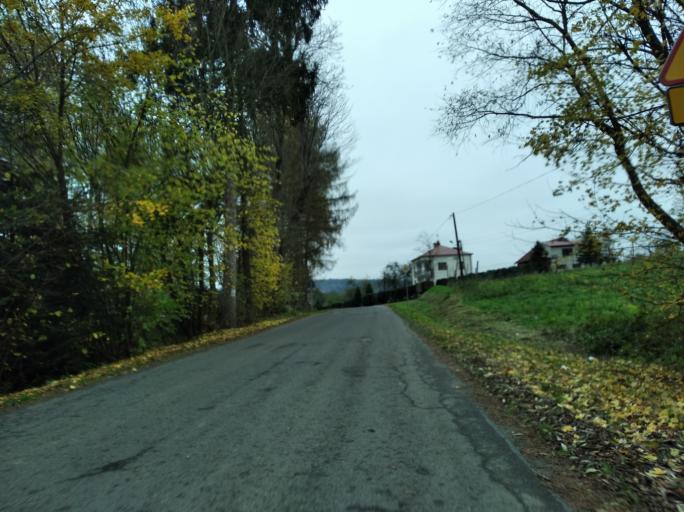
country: PL
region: Subcarpathian Voivodeship
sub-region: Powiat strzyzowski
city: Frysztak
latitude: 49.8367
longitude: 21.6235
